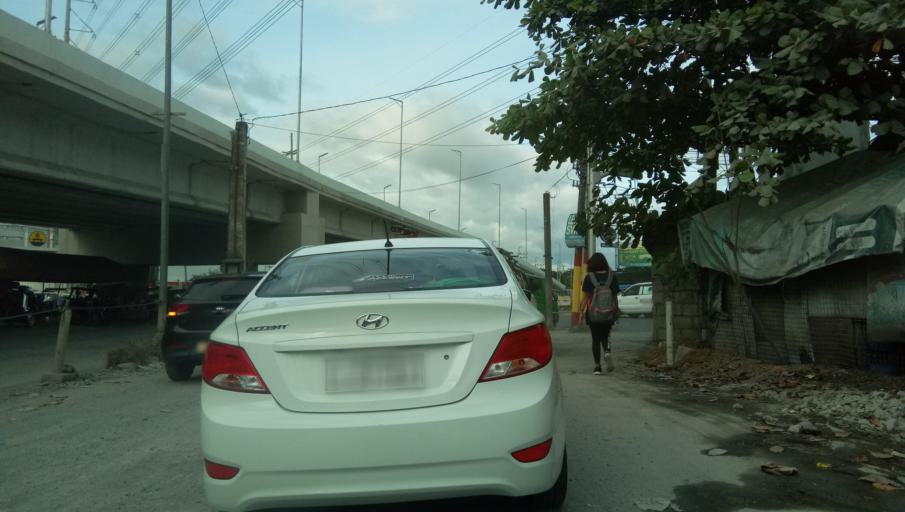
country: PH
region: Calabarzon
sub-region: Province of Cavite
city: Dasmarinas
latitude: 14.3712
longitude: 120.9385
